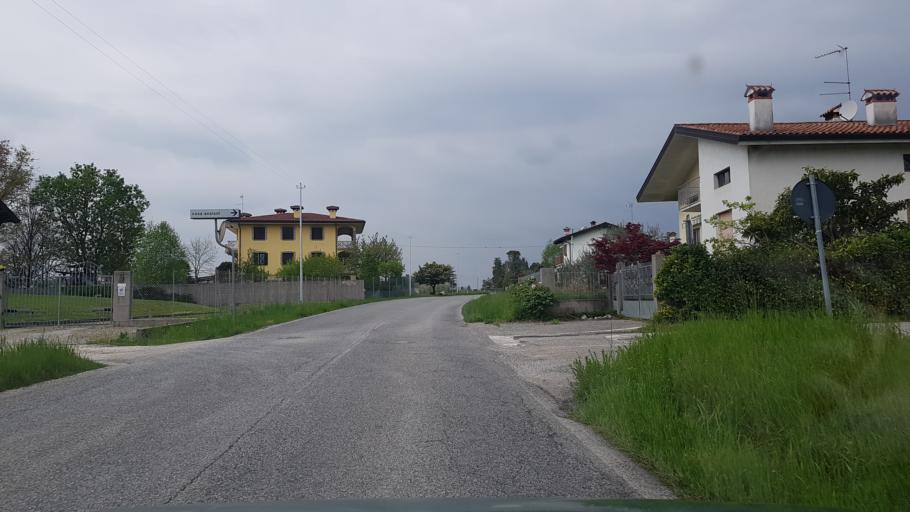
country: IT
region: Friuli Venezia Giulia
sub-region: Provincia di Udine
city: Faedis
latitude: 46.1295
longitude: 13.3566
